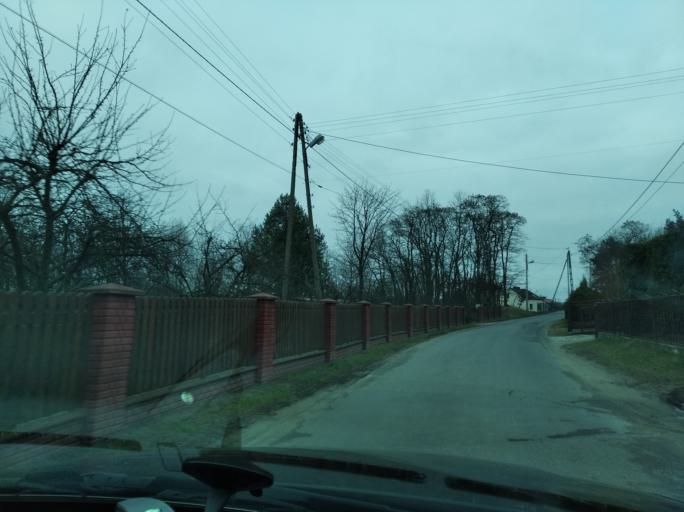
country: PL
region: Subcarpathian Voivodeship
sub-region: Powiat lancucki
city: Rakszawa
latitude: 50.1543
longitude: 22.2322
